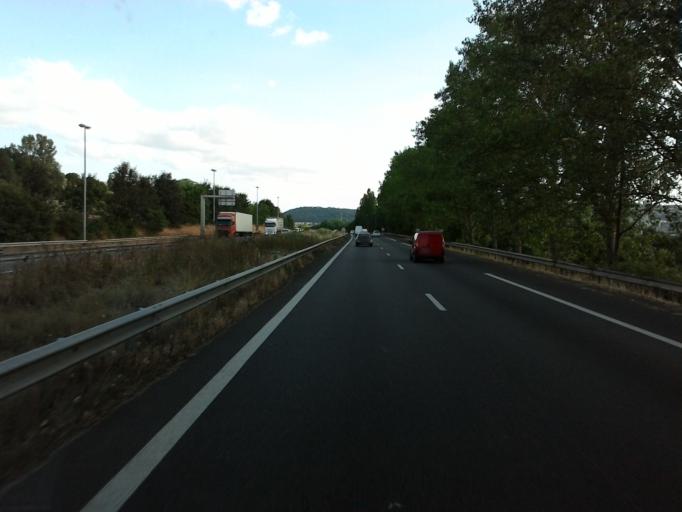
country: FR
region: Lorraine
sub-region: Departement de Meurthe-et-Moselle
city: Custines
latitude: 48.7754
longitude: 6.1440
